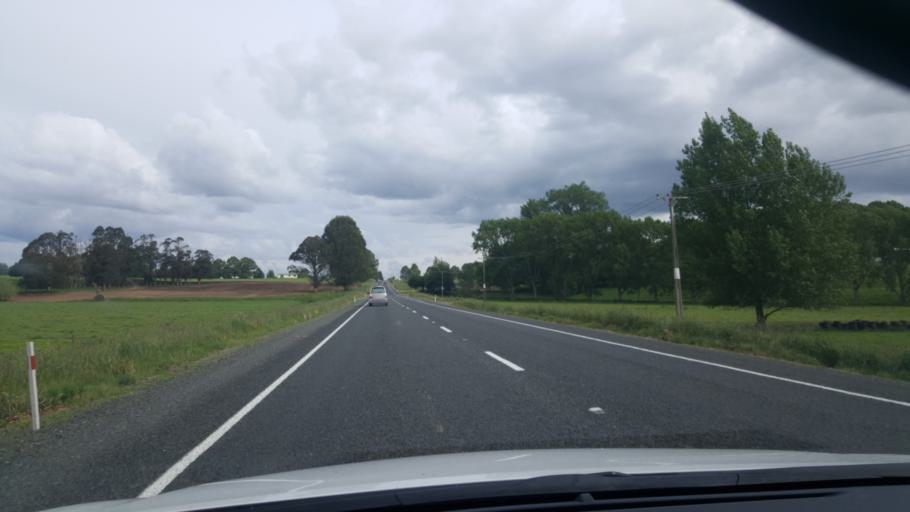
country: NZ
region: Waikato
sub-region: Taupo District
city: Taupo
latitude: -38.4906
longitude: 176.2921
